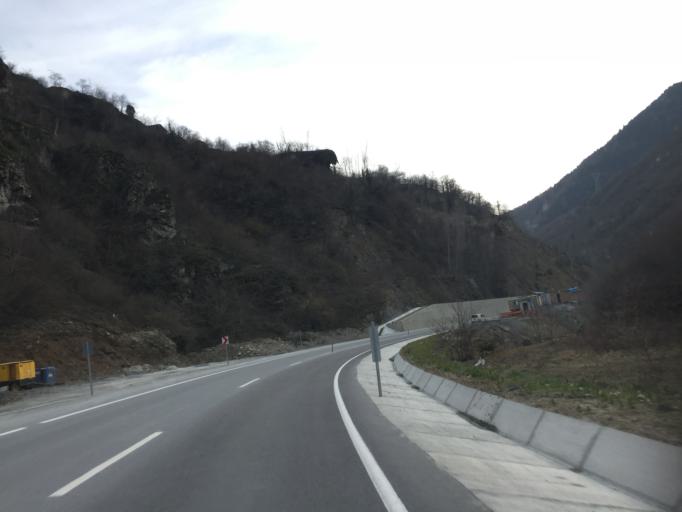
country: TR
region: Trabzon
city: Macka
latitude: 40.7683
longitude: 39.5656
